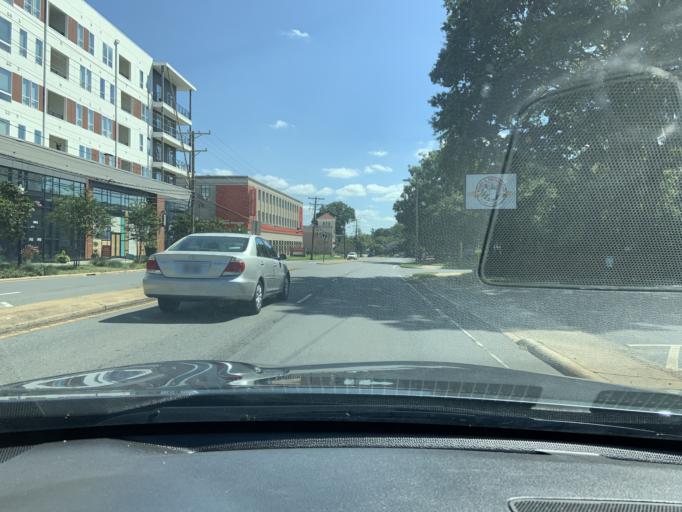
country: US
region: North Carolina
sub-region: Mecklenburg County
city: Charlotte
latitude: 35.1672
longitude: -80.8507
